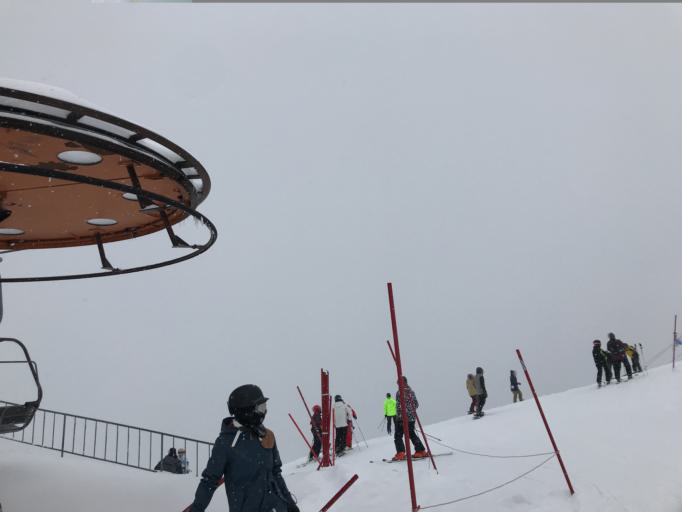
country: JP
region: Nagano
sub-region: Kitaazumi Gun
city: Hakuba
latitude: 36.6989
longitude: 137.8092
